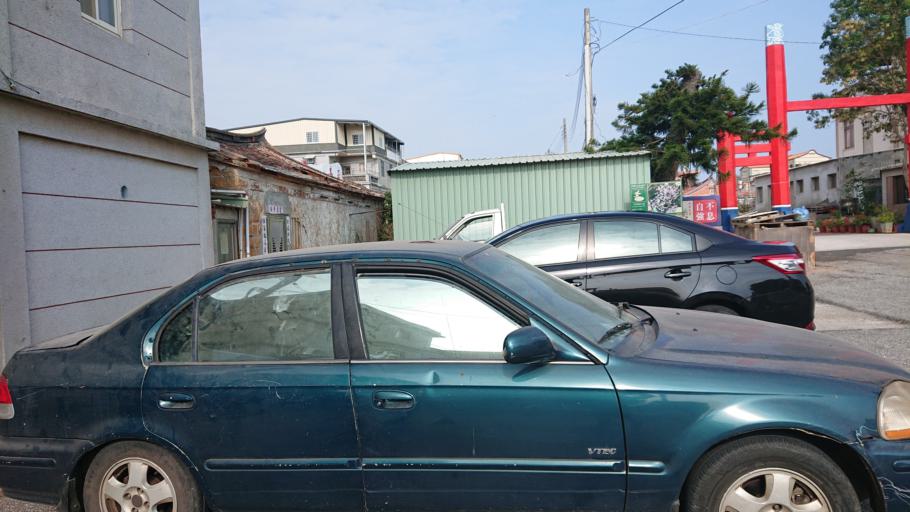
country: TW
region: Fukien
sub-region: Kinmen
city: Jincheng
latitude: 24.4790
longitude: 118.4271
